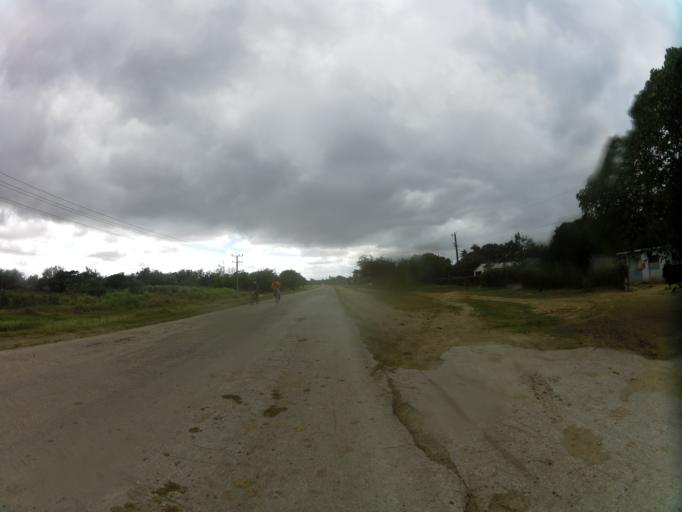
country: CU
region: Las Tunas
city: Las Tunas
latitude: 21.0475
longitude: -76.9315
